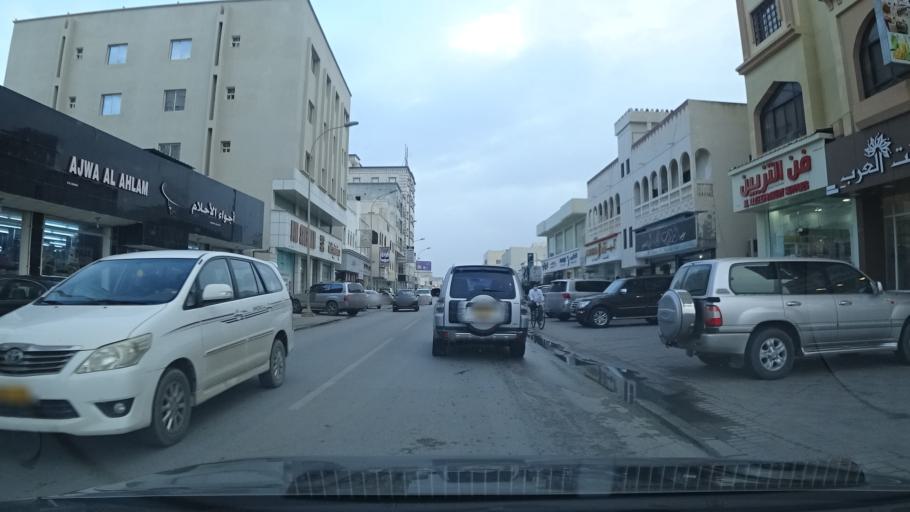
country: OM
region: Zufar
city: Salalah
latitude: 17.0100
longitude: 54.0820
